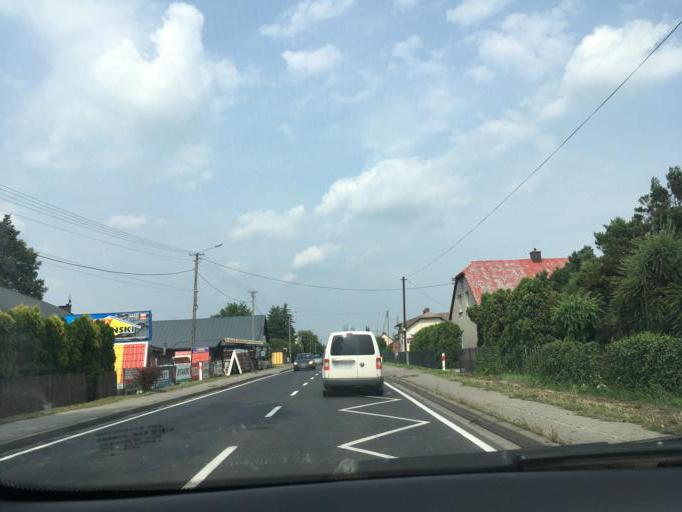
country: PL
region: Lesser Poland Voivodeship
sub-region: Powiat oswiecimski
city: Babice
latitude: 50.0517
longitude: 19.2028
